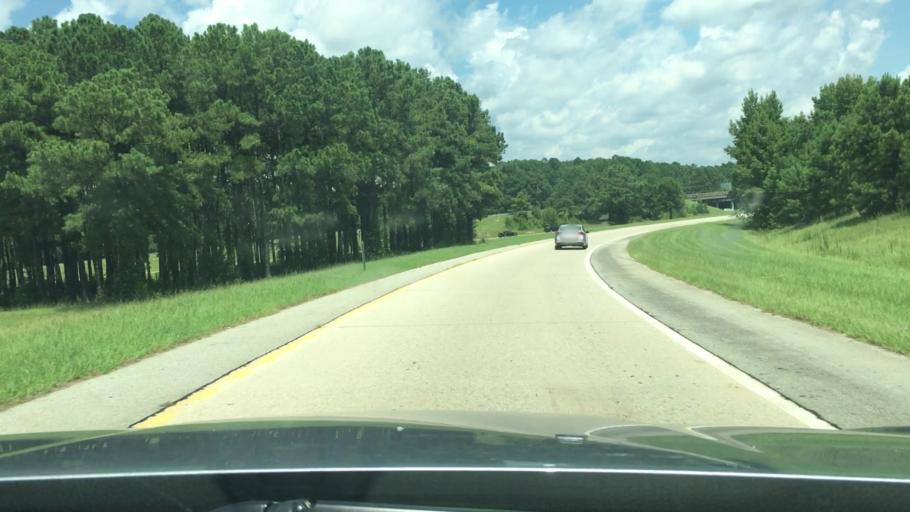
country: US
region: South Carolina
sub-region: Florence County
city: Florence
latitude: 34.1931
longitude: -79.8413
